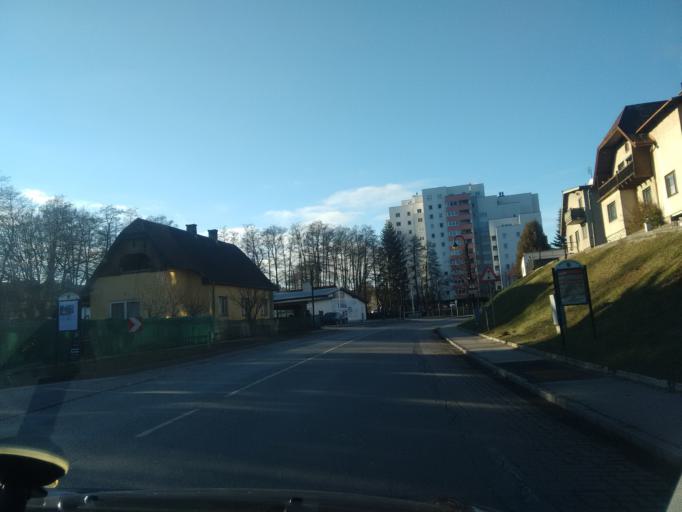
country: AT
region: Lower Austria
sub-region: Politischer Bezirk Wien-Umgebung
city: Pressbaum
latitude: 48.1774
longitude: 16.0588
